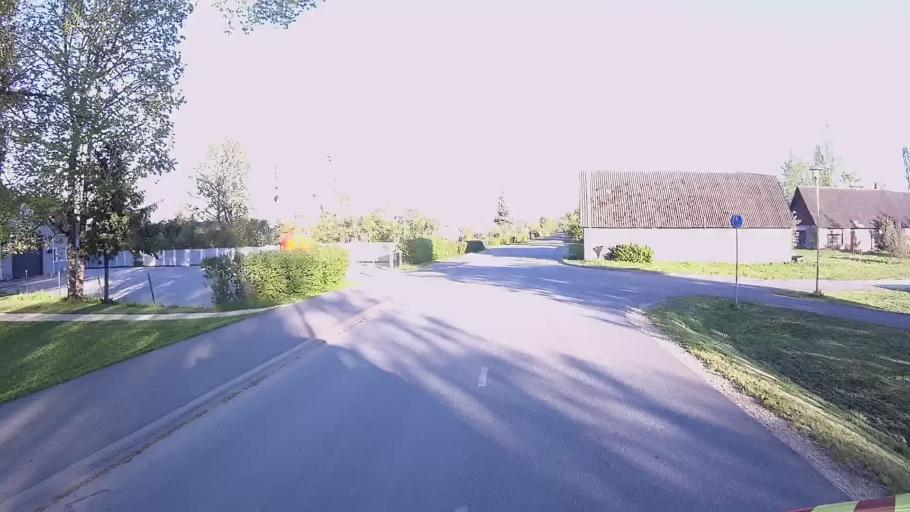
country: EE
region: Jogevamaa
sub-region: Poltsamaa linn
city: Poltsamaa
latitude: 58.5323
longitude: 25.9460
